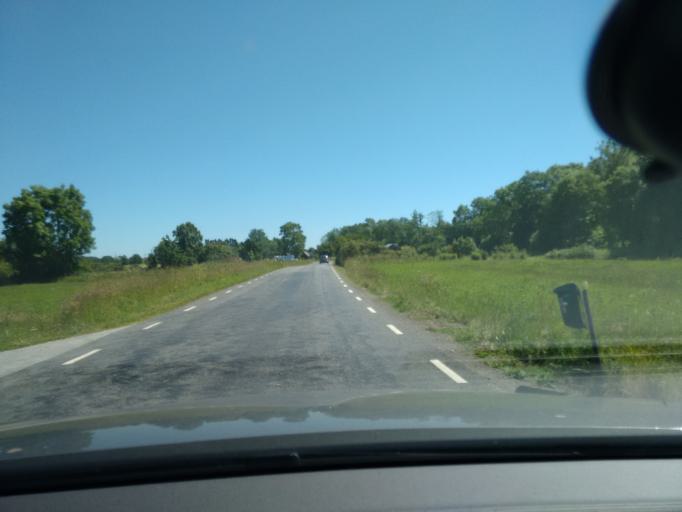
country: SE
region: Skane
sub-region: Kristianstads Kommun
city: Degeberga
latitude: 55.7796
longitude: 14.0854
